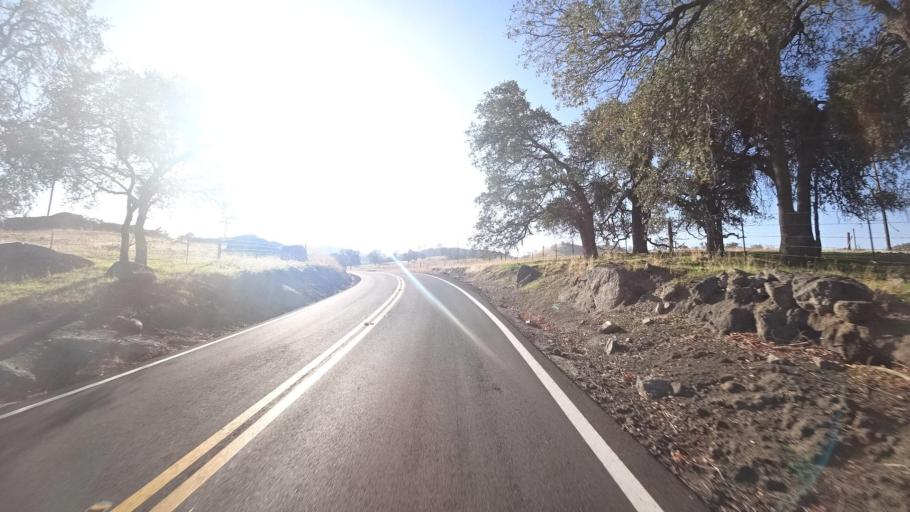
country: US
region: California
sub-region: Tulare County
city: Richgrove
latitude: 35.7314
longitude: -118.8595
